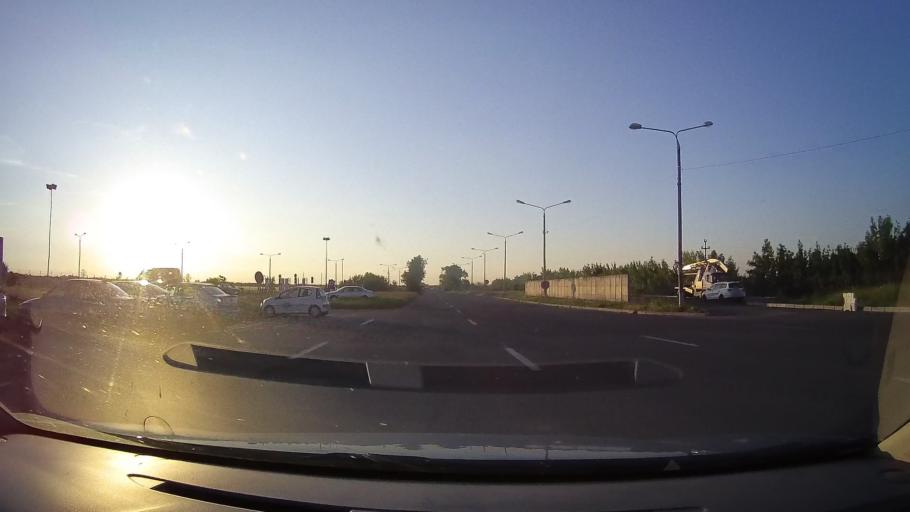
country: RO
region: Timis
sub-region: Comuna Moravita
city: Moravita
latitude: 45.2332
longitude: 21.2718
